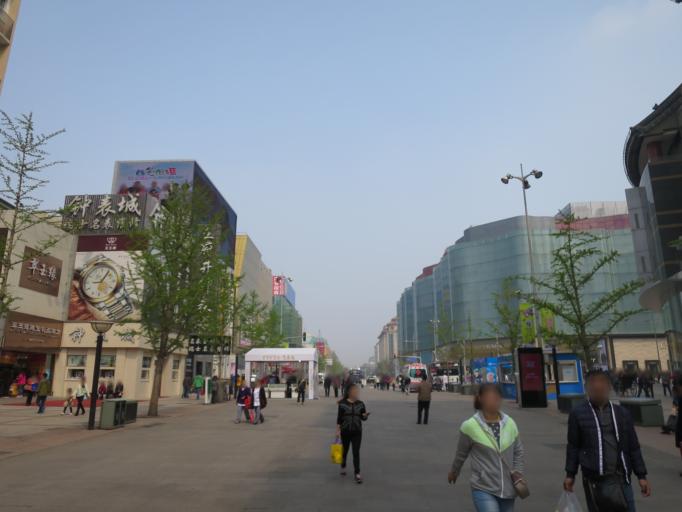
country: CN
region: Beijing
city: Beijing
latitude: 39.9133
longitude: 116.4051
